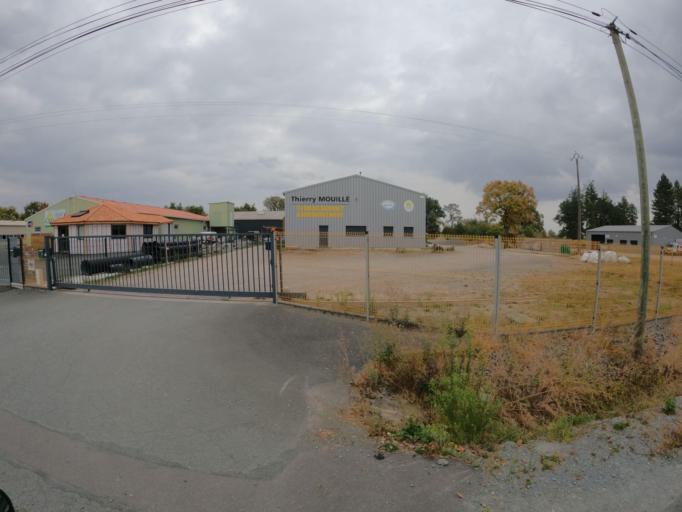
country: FR
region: Pays de la Loire
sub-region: Departement de la Vendee
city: Tiffauges
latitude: 47.0059
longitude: -1.1024
